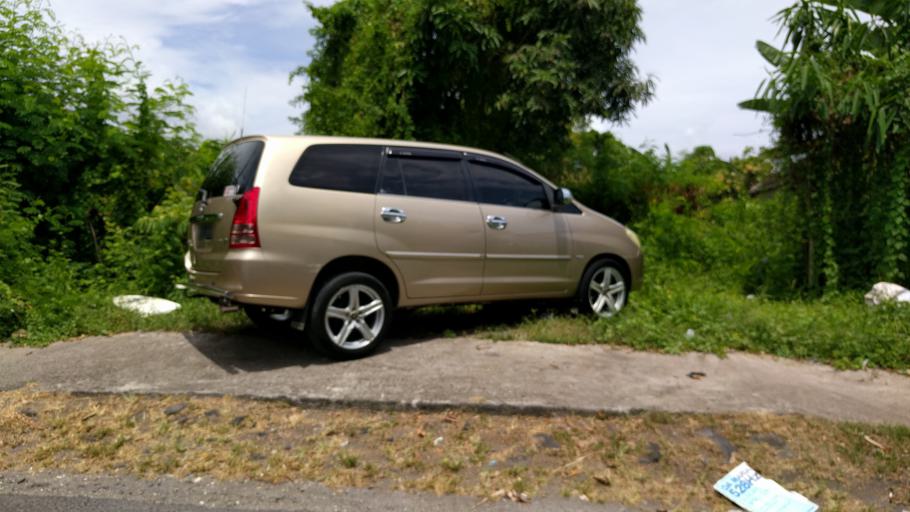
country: ID
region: Bali
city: Banjar Gunungpande
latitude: -8.6553
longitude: 115.1478
